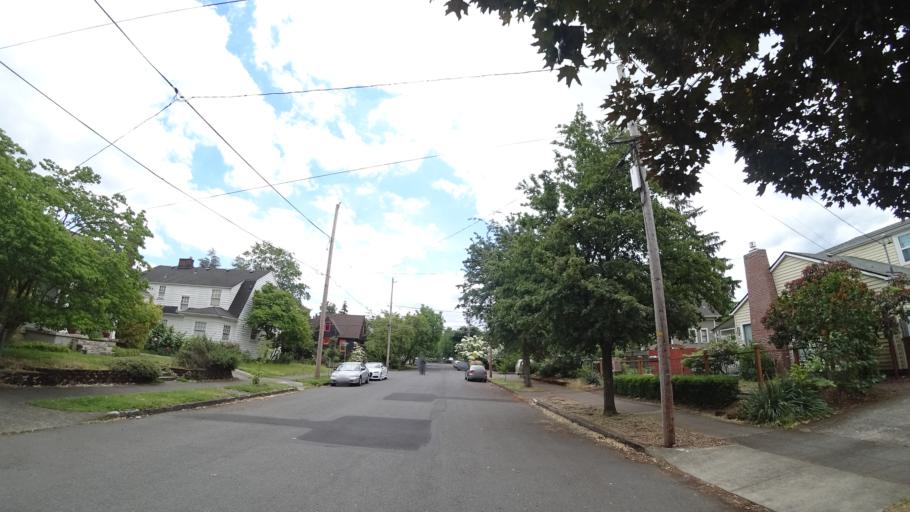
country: US
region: Oregon
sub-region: Multnomah County
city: Portland
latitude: 45.5660
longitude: -122.6739
